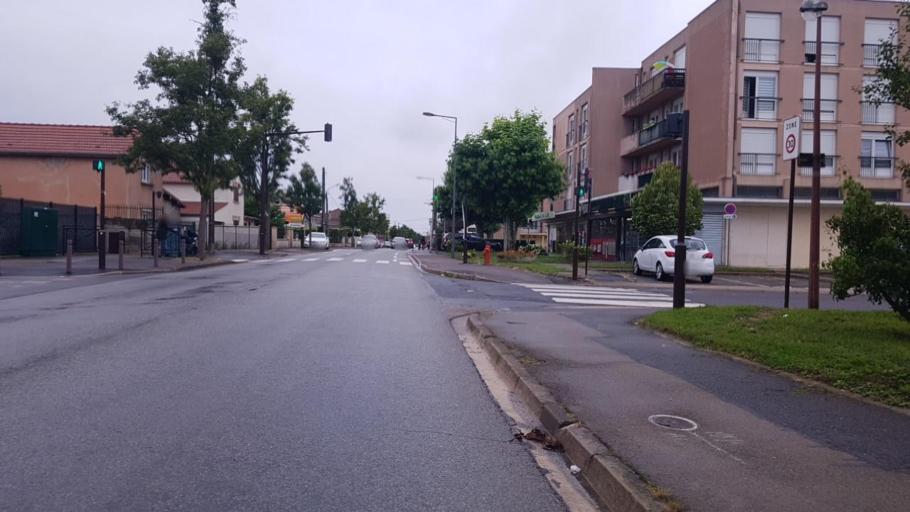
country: FR
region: Champagne-Ardenne
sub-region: Departement de la Marne
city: Saint-Memmie
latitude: 48.9364
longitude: 4.3857
